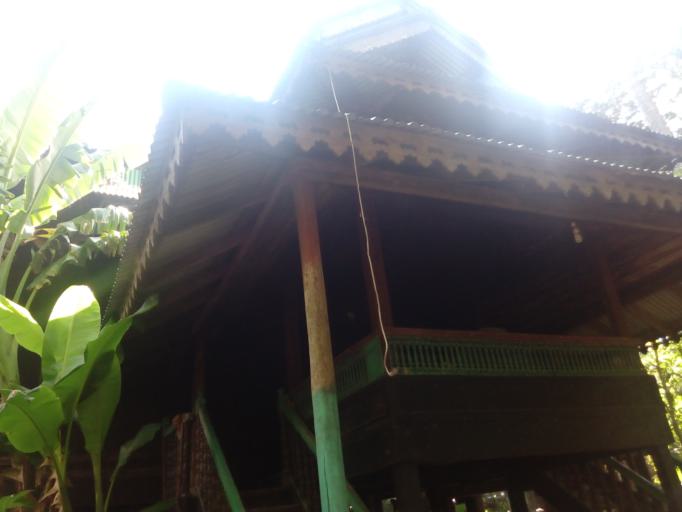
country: BD
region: Chittagong
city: Cox's Bazar
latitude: 21.4162
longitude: 92.1050
